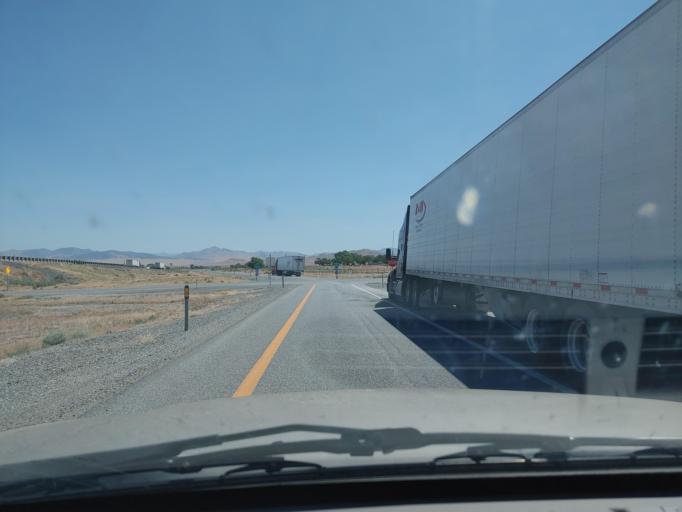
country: US
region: Nevada
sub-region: Humboldt County
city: Winnemucca
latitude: 40.6564
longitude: -118.1465
